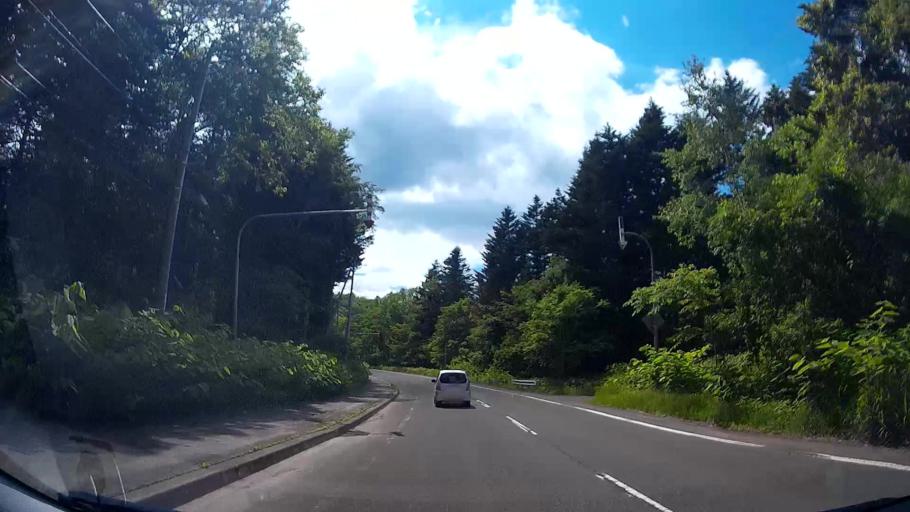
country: JP
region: Hokkaido
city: Kitahiroshima
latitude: 42.8435
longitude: 141.4695
